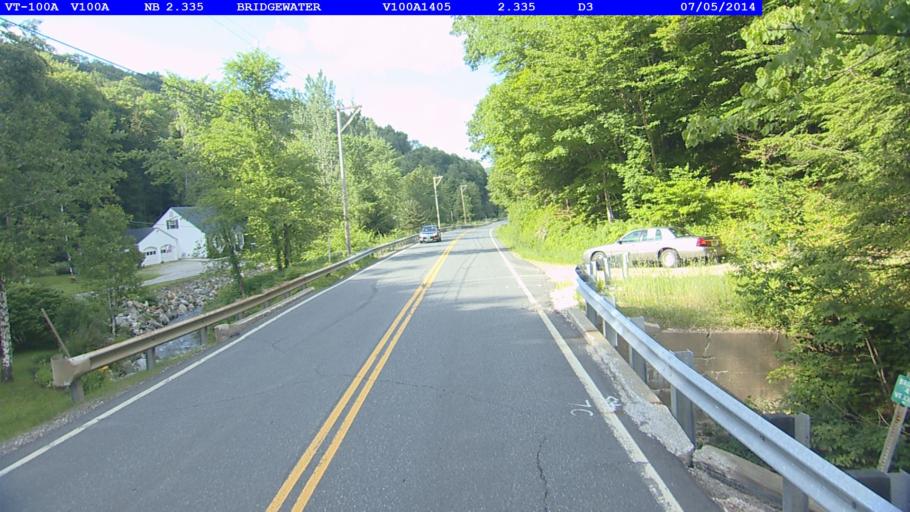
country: US
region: Vermont
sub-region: Windsor County
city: Woodstock
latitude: 43.5485
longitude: -72.7103
